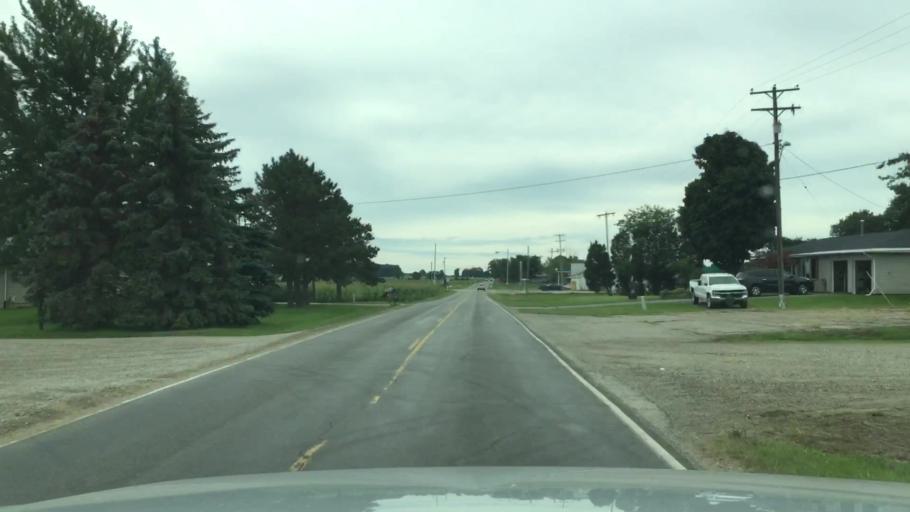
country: US
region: Michigan
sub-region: Shiawassee County
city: Durand
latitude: 43.0019
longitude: -83.9869
